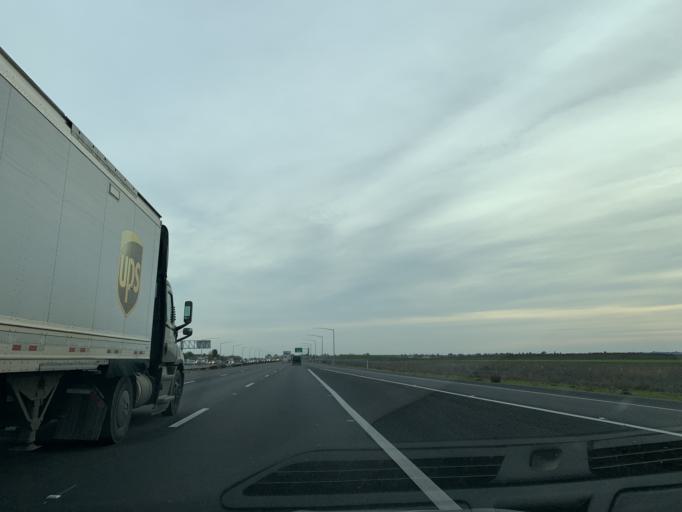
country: US
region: California
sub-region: Sacramento County
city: Elverta
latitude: 38.6832
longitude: -121.5403
